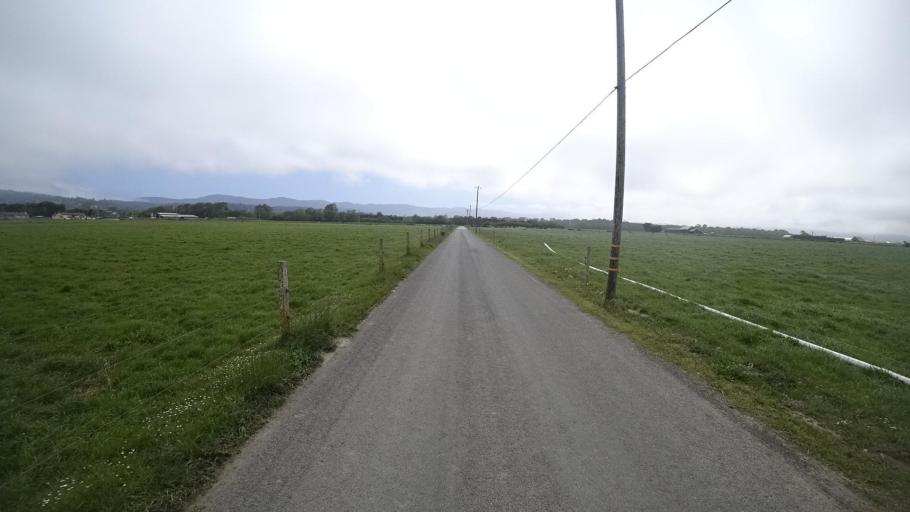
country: US
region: California
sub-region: Humboldt County
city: Fortuna
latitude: 40.5917
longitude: -124.1954
